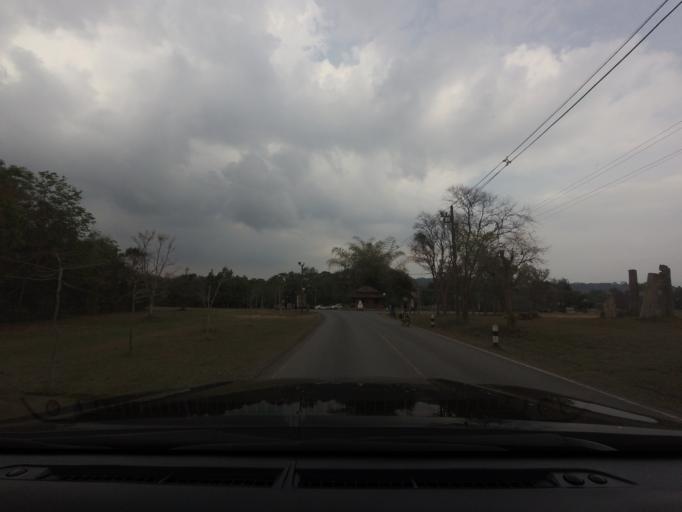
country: TH
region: Nakhon Nayok
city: Nakhon Nayok
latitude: 14.4331
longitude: 101.3714
